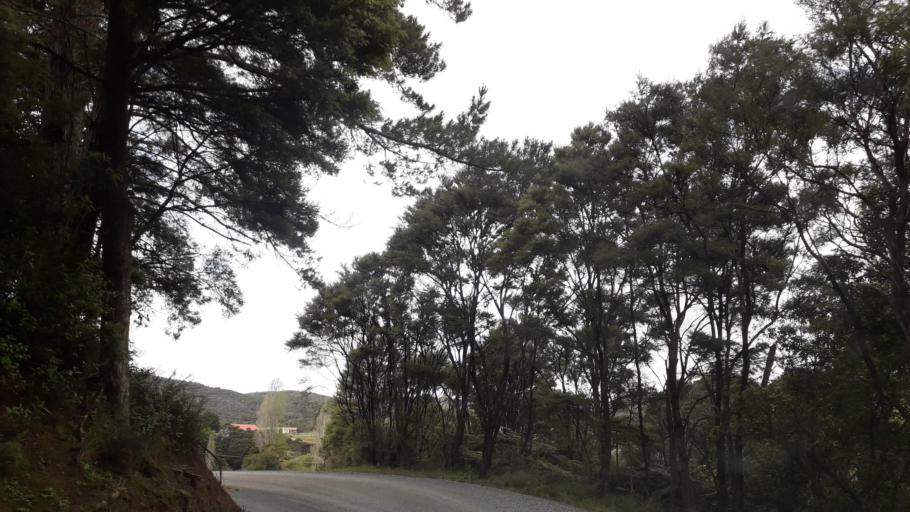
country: NZ
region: Northland
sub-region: Far North District
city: Taipa
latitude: -35.0469
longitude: 173.5611
